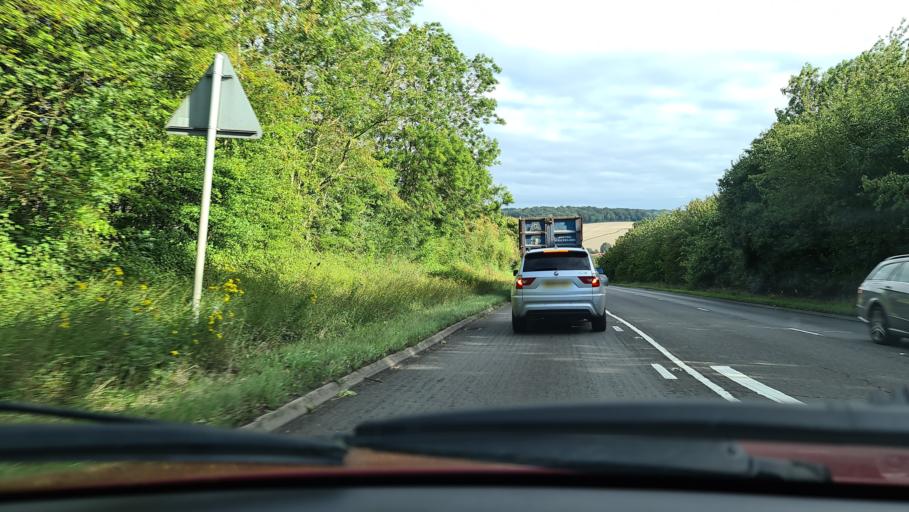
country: GB
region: England
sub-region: Buckinghamshire
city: Amersham
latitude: 51.6586
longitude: -0.6141
